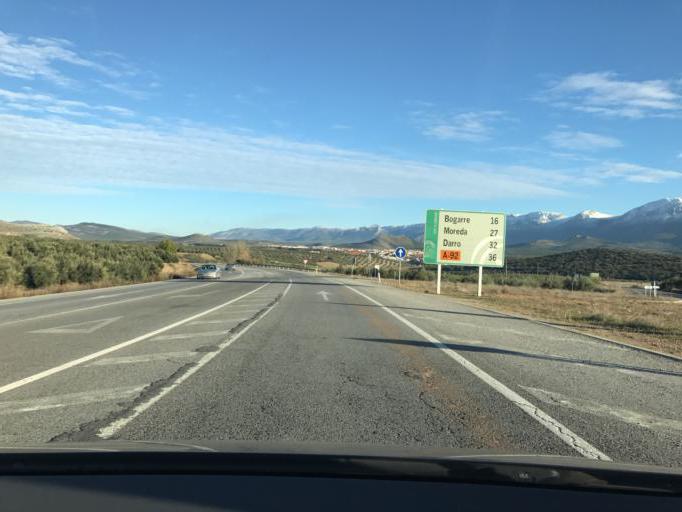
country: ES
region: Andalusia
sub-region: Provincia de Granada
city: Iznalloz
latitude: 37.3997
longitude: -3.5516
